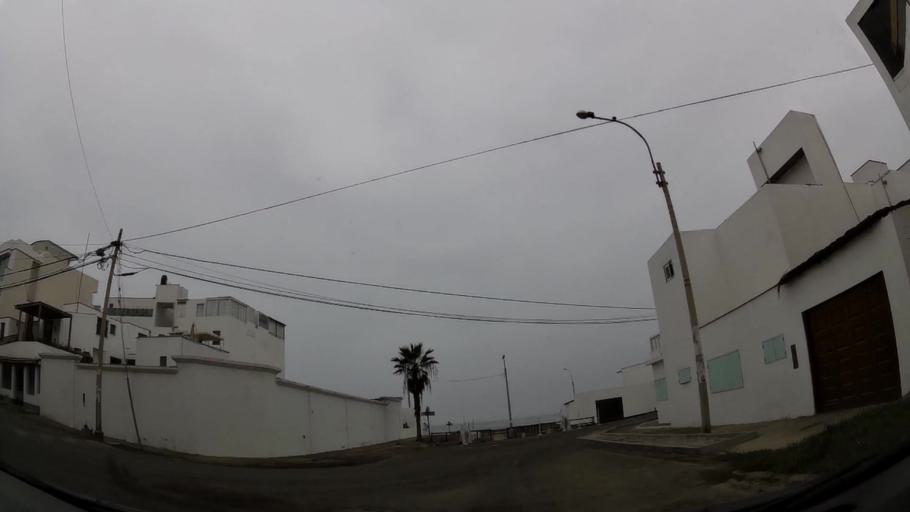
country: PE
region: Lima
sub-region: Lima
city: Punta Hermosa
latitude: -12.3354
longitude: -76.8279
